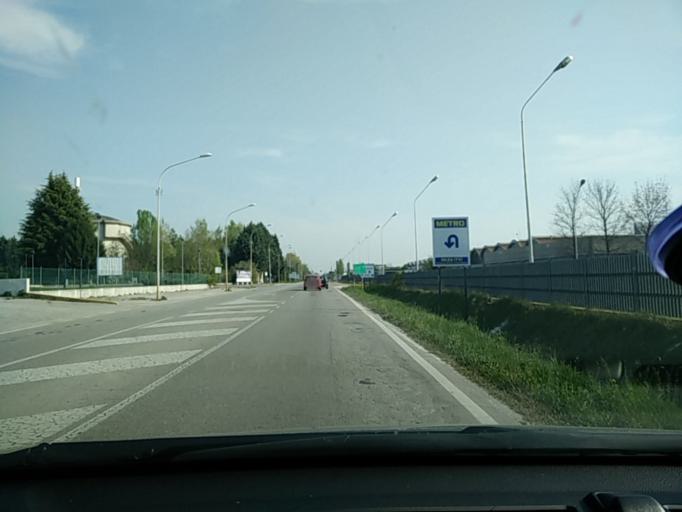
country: IT
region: Friuli Venezia Giulia
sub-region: Provincia di Pordenone
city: Azzano Decimo
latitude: 45.9318
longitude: 12.6461
